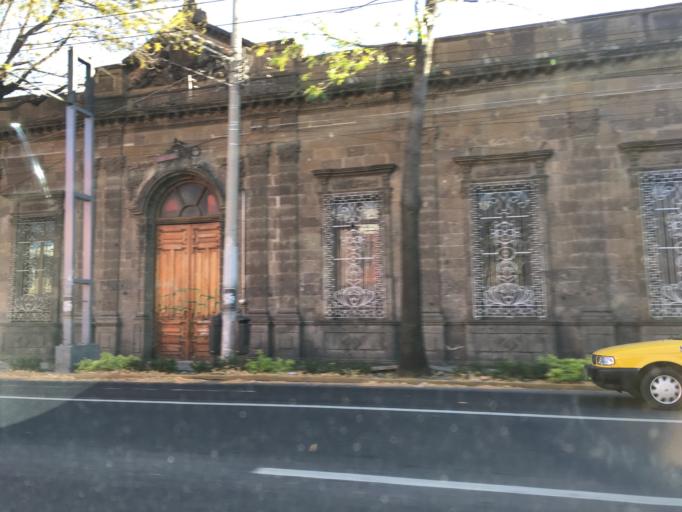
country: MX
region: Jalisco
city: Guadalajara
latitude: 20.6772
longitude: -103.3562
